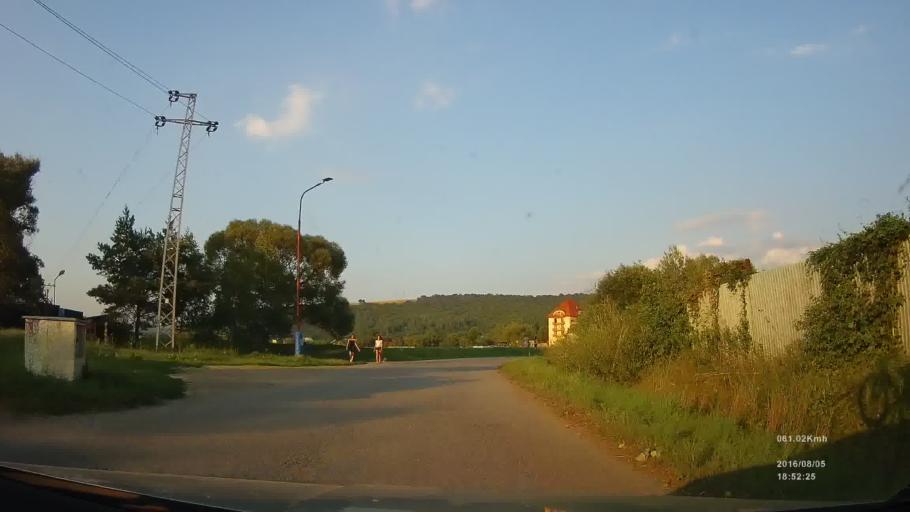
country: SK
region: Presovsky
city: Stropkov
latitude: 49.2141
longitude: 21.6518
